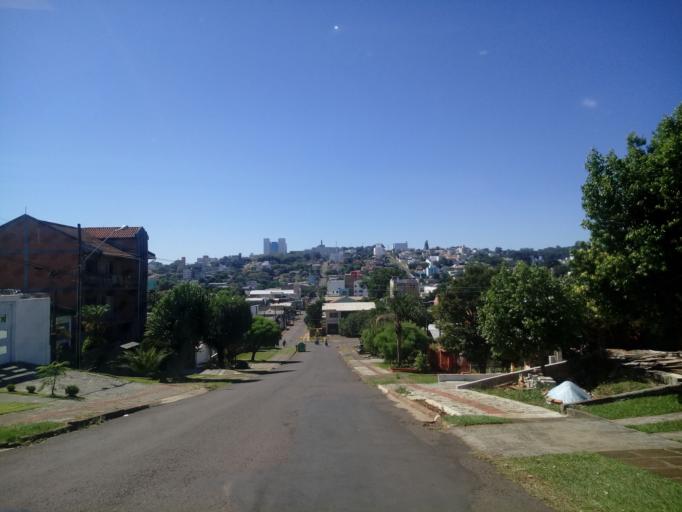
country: BR
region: Santa Catarina
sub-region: Chapeco
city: Chapeco
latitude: -27.1108
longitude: -52.6087
